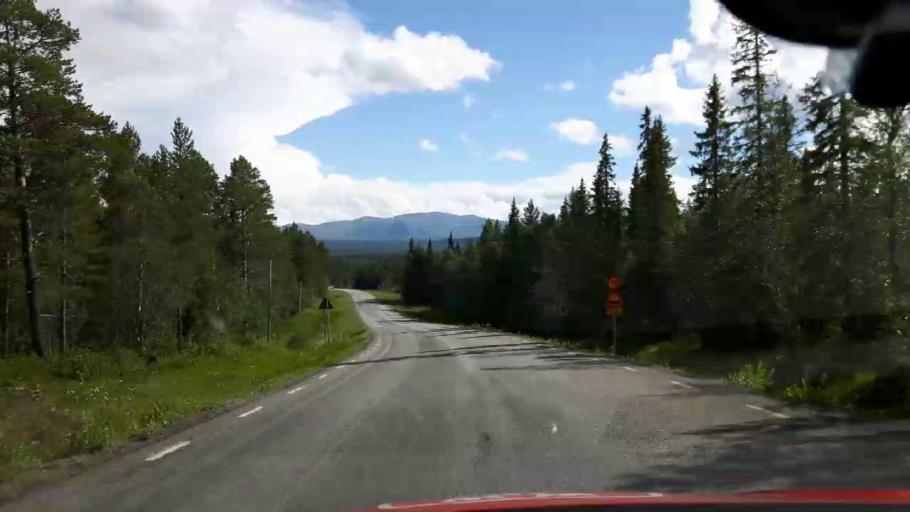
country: SE
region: Jaemtland
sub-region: Are Kommun
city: Are
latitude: 63.2275
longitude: 13.1593
